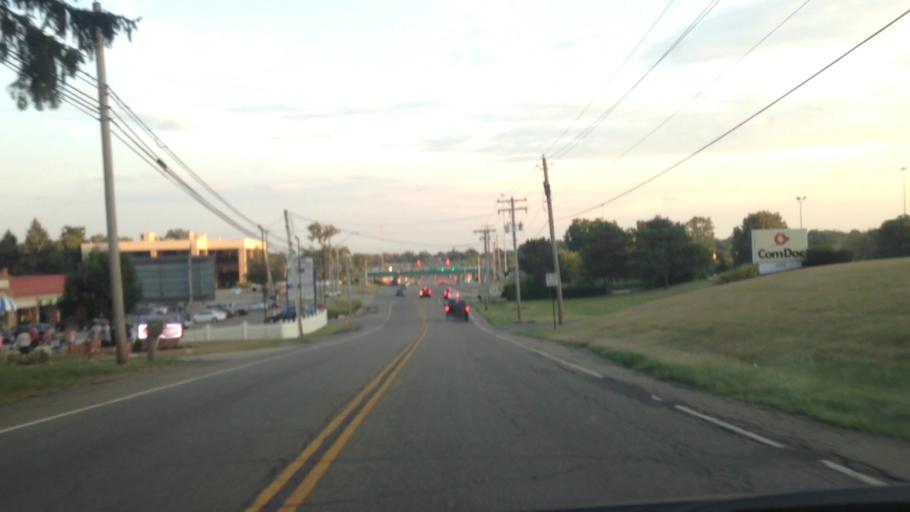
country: US
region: Ohio
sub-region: Summit County
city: Green
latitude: 40.9682
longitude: -81.4649
